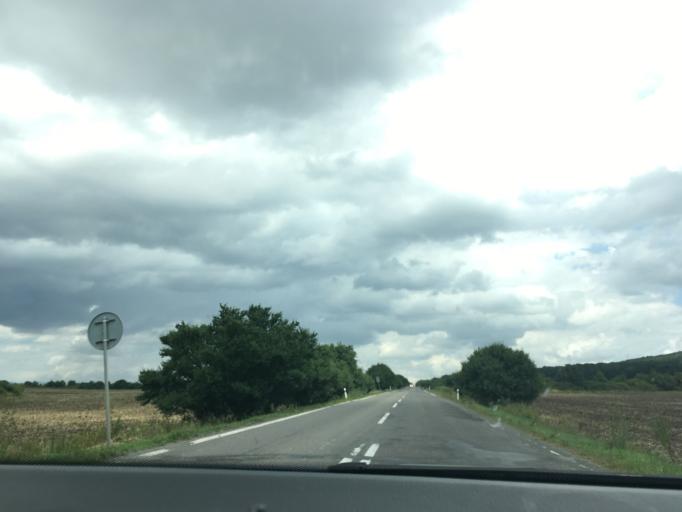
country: HU
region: Borsod-Abauj-Zemplen
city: Satoraljaujhely
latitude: 48.4913
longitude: 21.6486
